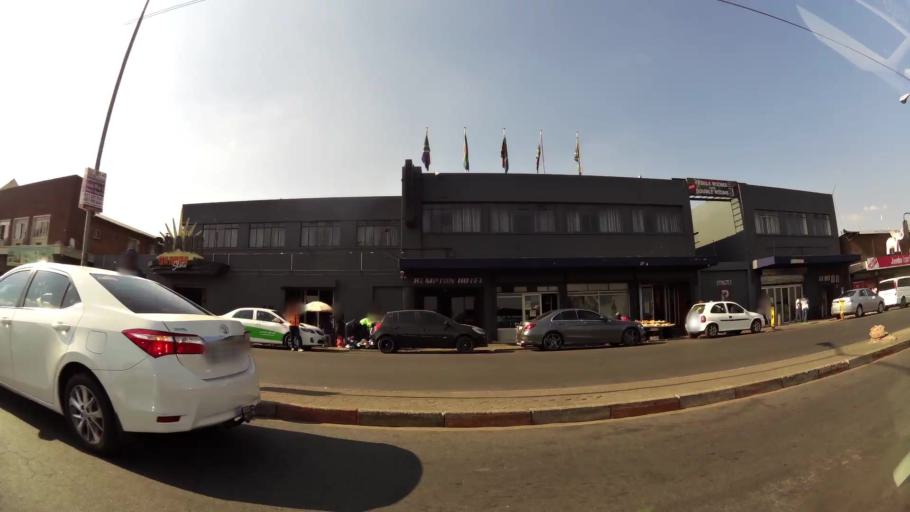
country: ZA
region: Gauteng
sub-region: City of Johannesburg Metropolitan Municipality
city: Modderfontein
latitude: -26.1087
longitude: 28.2288
